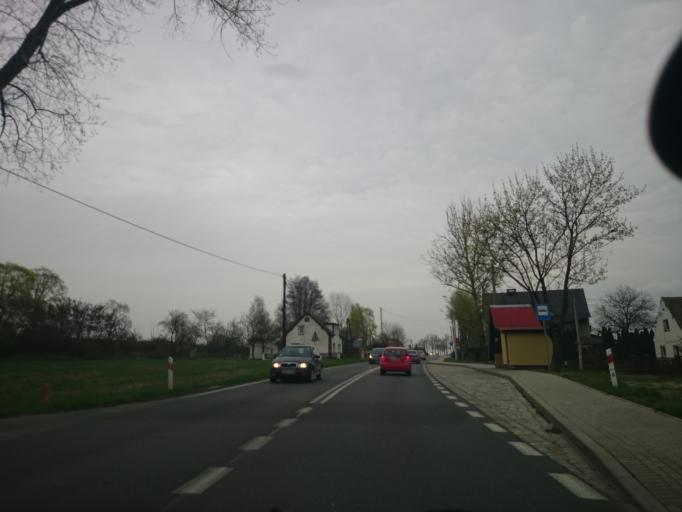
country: PL
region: Opole Voivodeship
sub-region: Powiat nyski
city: Otmuchow
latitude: 50.4687
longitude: 17.2158
